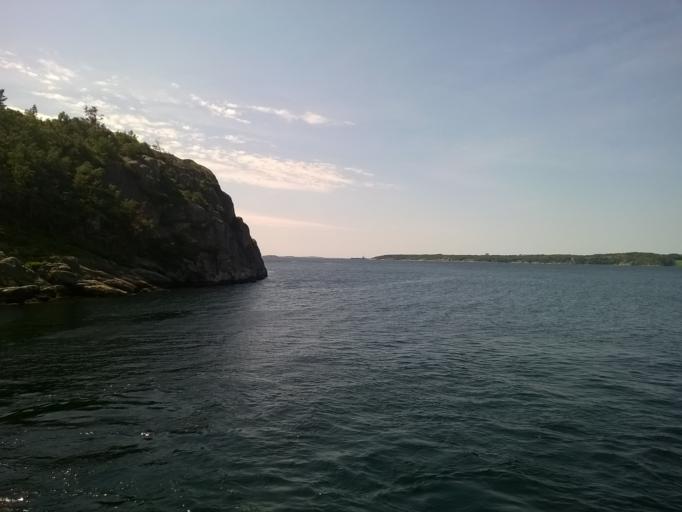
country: SE
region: Vaestra Goetaland
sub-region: Lysekils Kommun
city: Brastad
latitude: 58.3011
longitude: 11.5334
